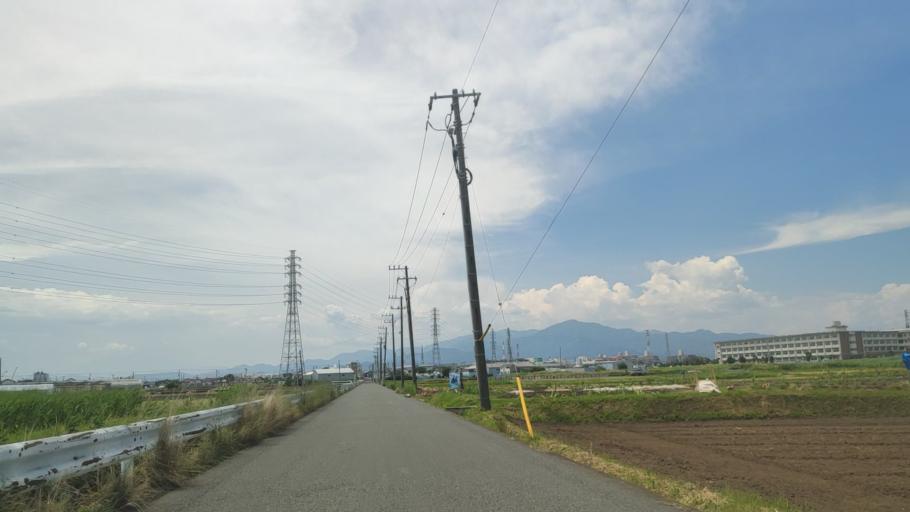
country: JP
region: Kanagawa
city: Chigasaki
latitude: 35.3562
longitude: 139.3901
